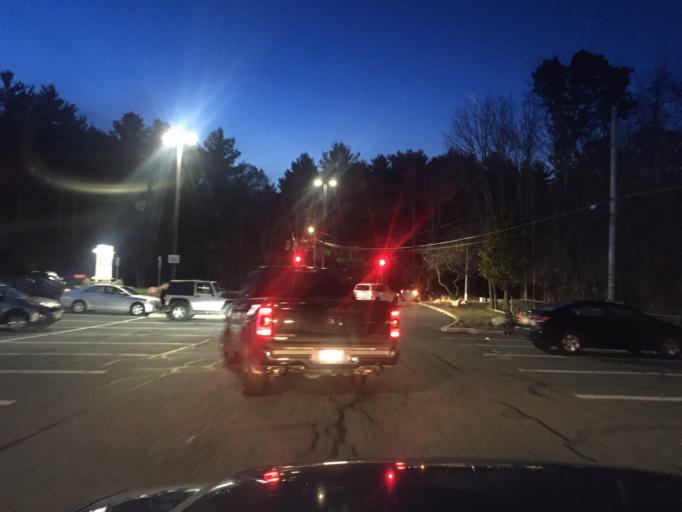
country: US
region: Massachusetts
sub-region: Norfolk County
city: Medfield
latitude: 42.1949
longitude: -71.2876
